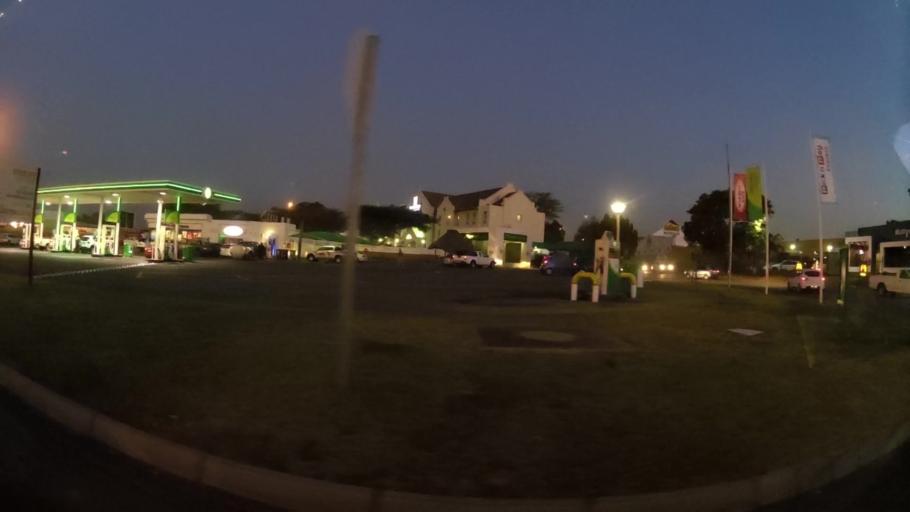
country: ZA
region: North-West
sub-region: Bojanala Platinum District Municipality
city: Rustenburg
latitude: -25.7030
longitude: 27.2542
